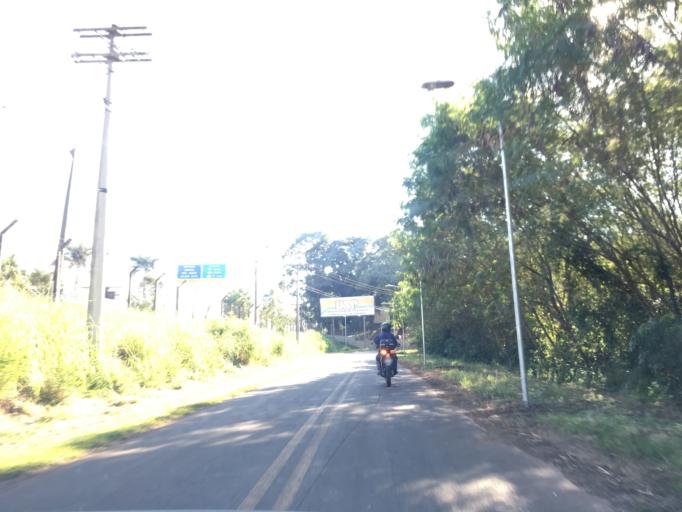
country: BR
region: Sao Paulo
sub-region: Piracicaba
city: Piracicaba
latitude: -22.7158
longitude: -47.6278
